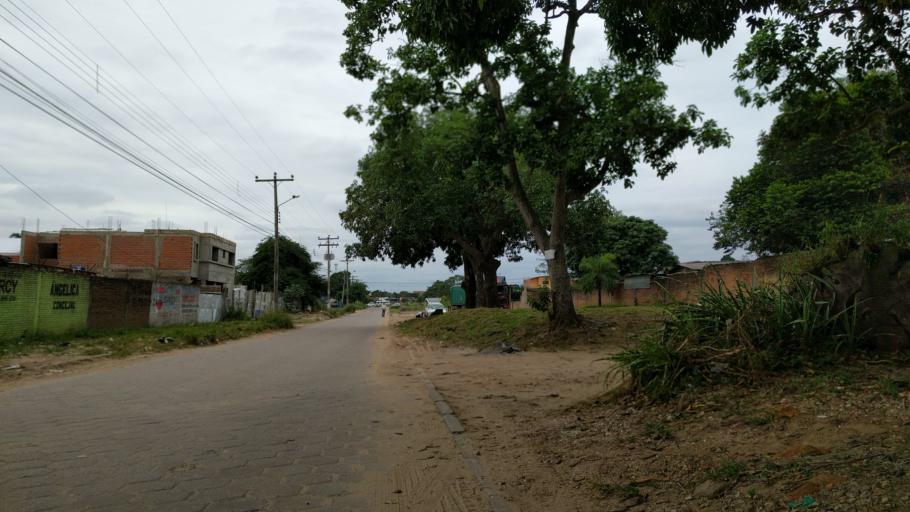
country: BO
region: Santa Cruz
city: Santa Cruz de la Sierra
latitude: -17.8056
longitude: -63.2164
